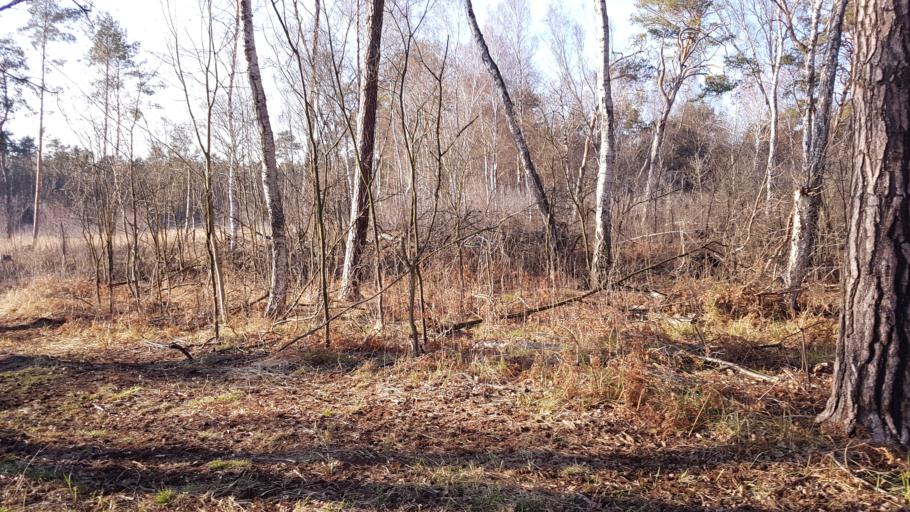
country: DE
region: Brandenburg
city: Schilda
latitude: 51.5807
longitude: 13.3970
